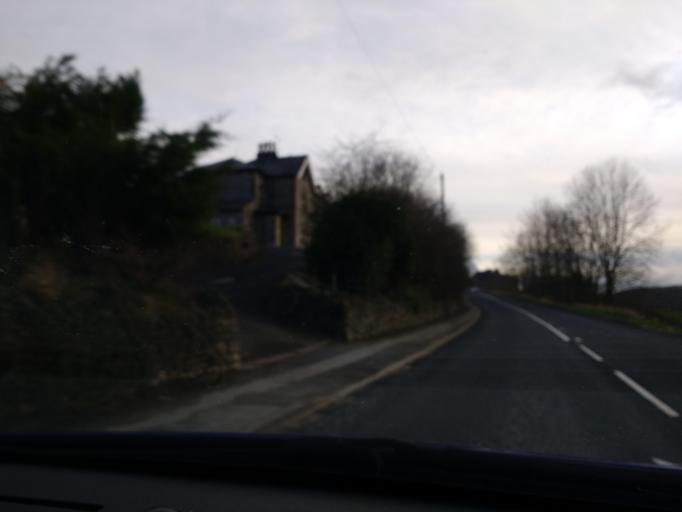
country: GB
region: England
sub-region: North Yorkshire
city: Settle
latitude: 54.0875
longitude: -2.2739
